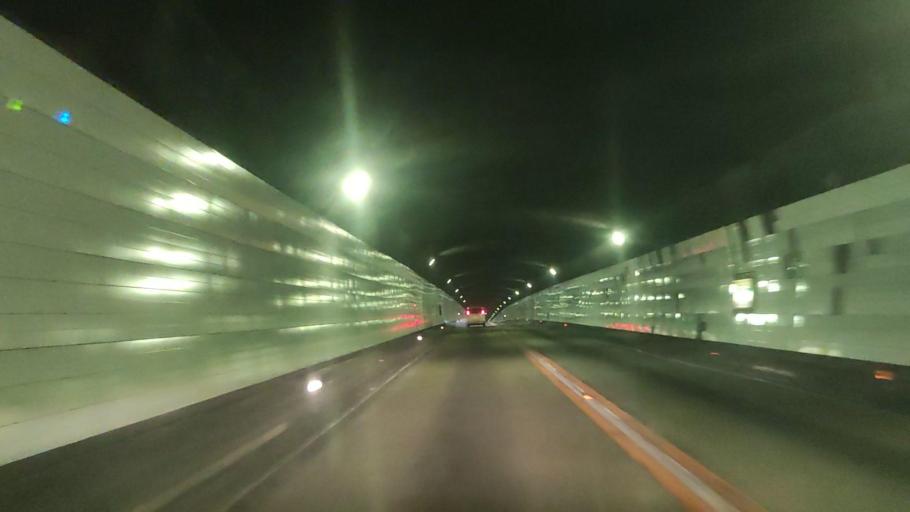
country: JP
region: Kumamoto
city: Hitoyoshi
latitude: 32.0980
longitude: 130.8035
